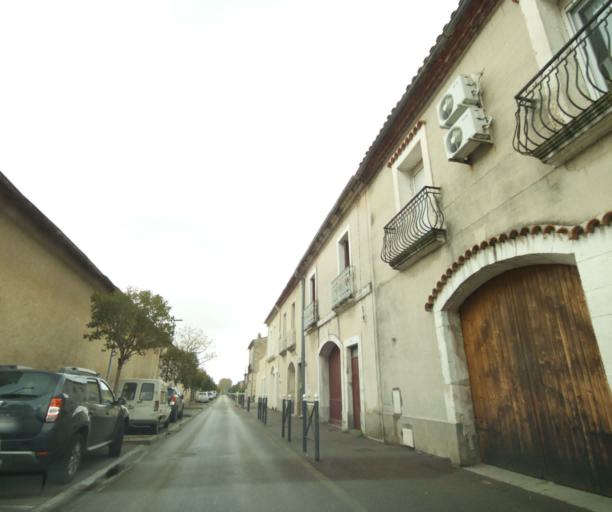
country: FR
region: Languedoc-Roussillon
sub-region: Departement de l'Herault
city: Cournonterral
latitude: 43.5553
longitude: 3.7223
